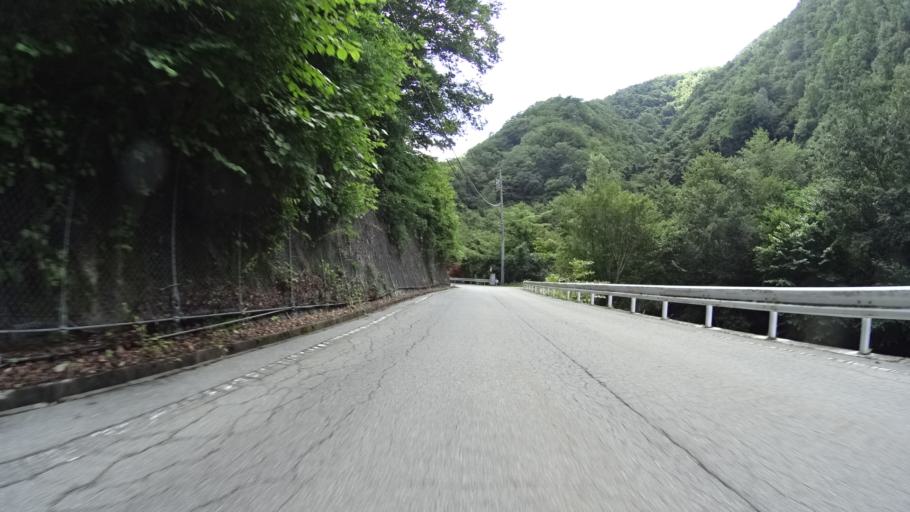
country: JP
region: Yamanashi
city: Enzan
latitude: 35.6712
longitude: 138.8065
